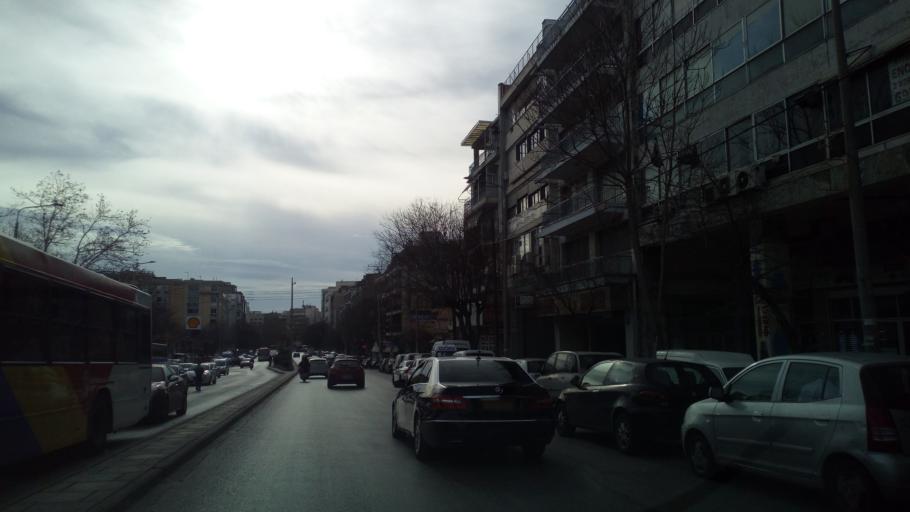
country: GR
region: Central Macedonia
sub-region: Nomos Thessalonikis
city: Thessaloniki
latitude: 40.6445
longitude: 22.9352
